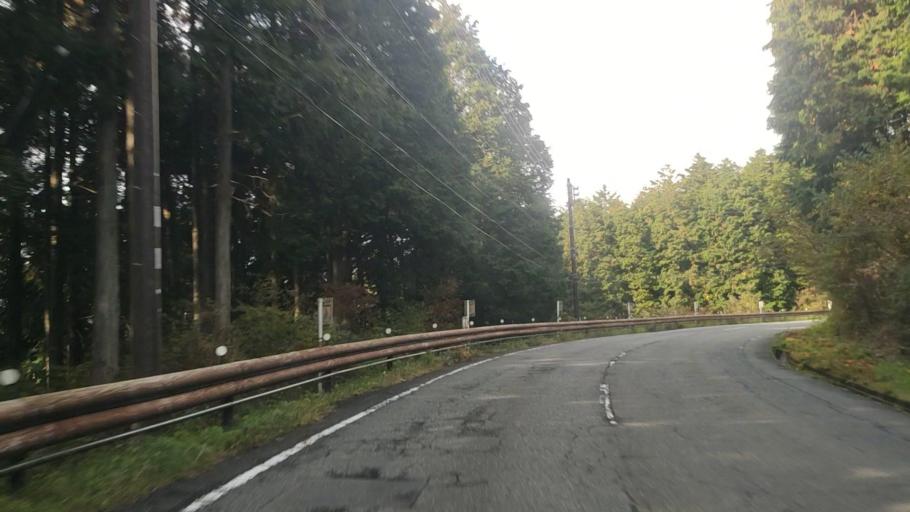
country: JP
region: Shizuoka
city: Fujinomiya
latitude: 35.2980
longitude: 138.6689
